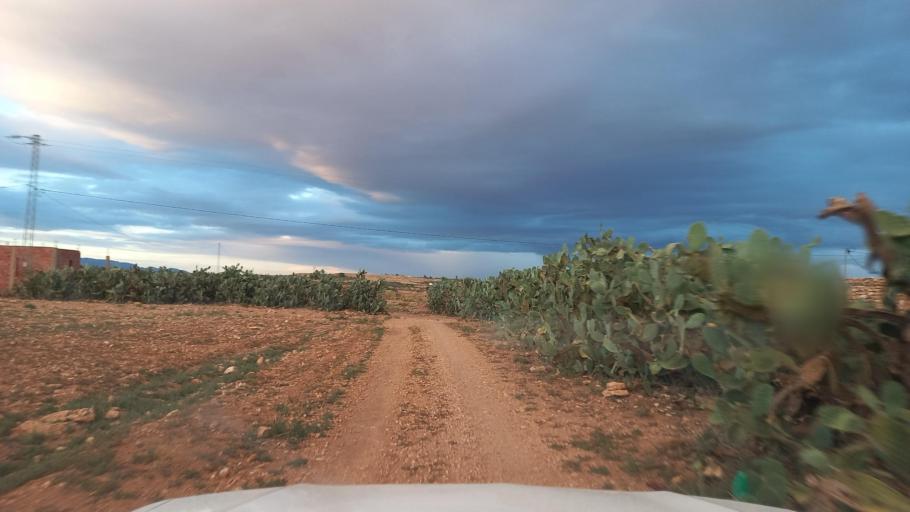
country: TN
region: Al Qasrayn
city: Kasserine
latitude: 35.2624
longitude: 8.9387
